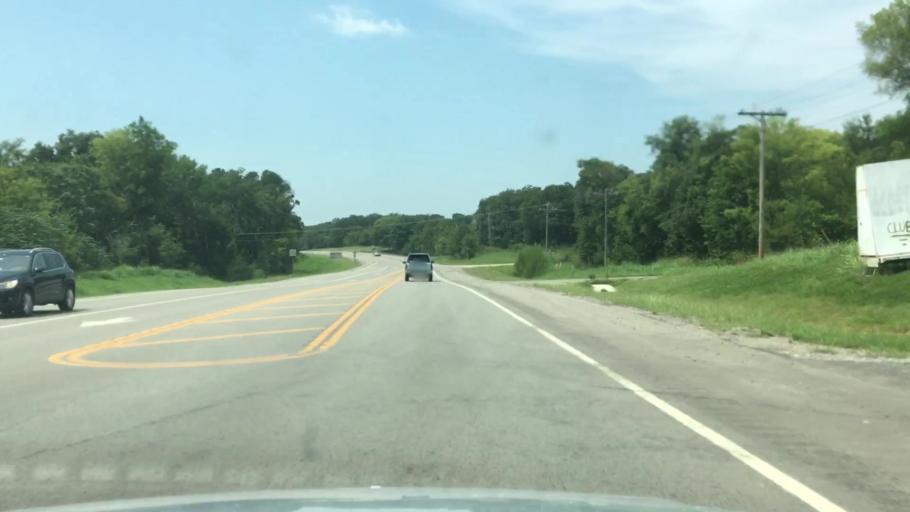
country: US
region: Oklahoma
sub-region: Wagoner County
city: Wagoner
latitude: 35.9297
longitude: -95.2505
